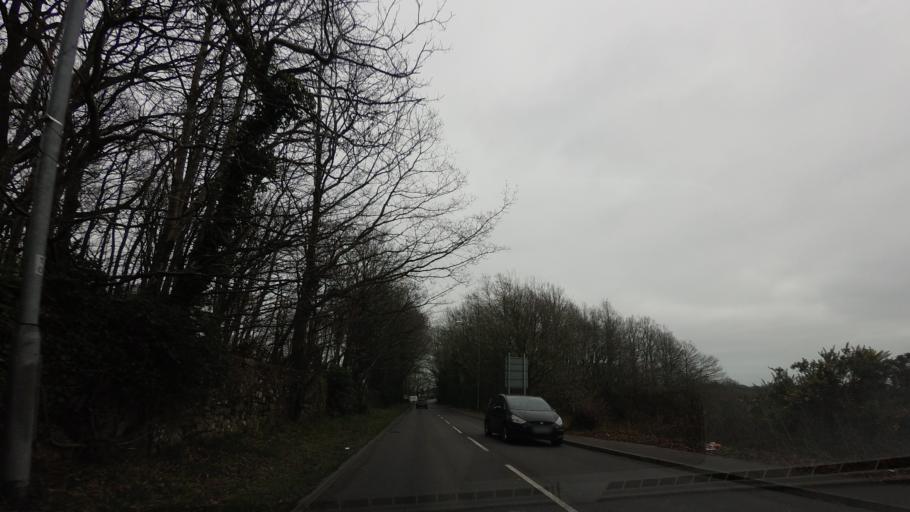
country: GB
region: England
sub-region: East Sussex
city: Saint Leonards-on-Sea
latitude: 50.8914
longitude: 0.5494
